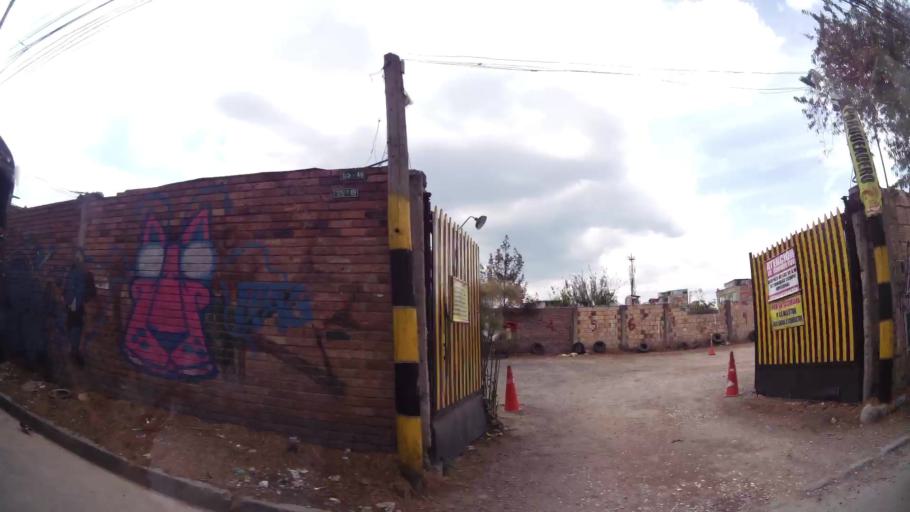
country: CO
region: Cundinamarca
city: Cota
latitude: 4.7263
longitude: -74.0932
